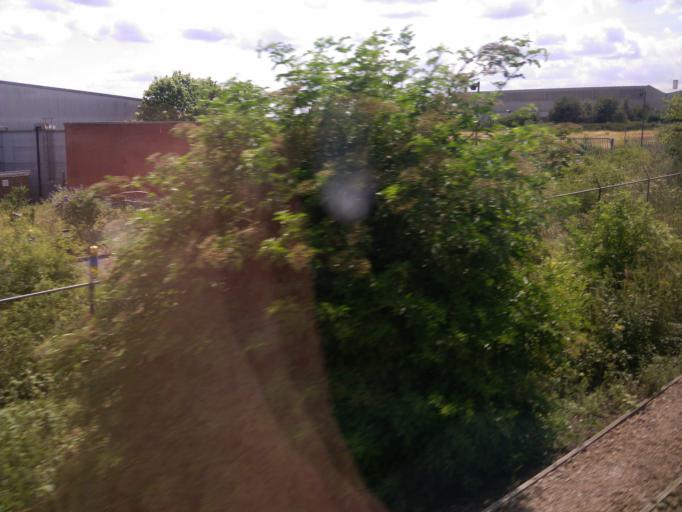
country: GB
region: England
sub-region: Essex
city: Witham
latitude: 51.8113
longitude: 0.6492
